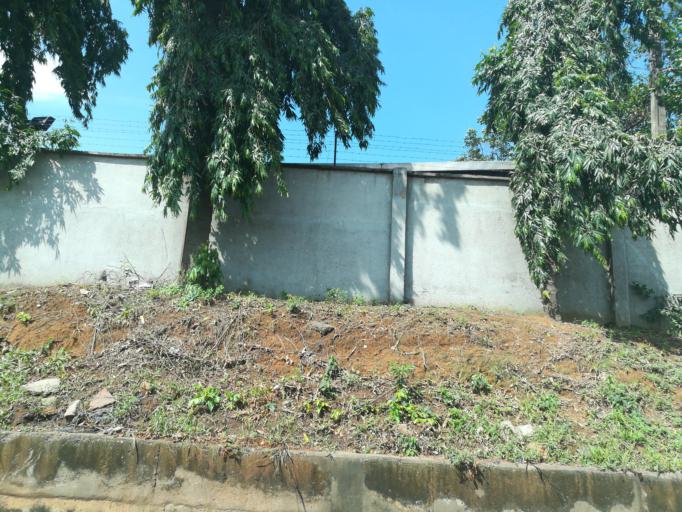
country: NG
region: Lagos
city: Agege
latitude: 6.6061
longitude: 3.3132
